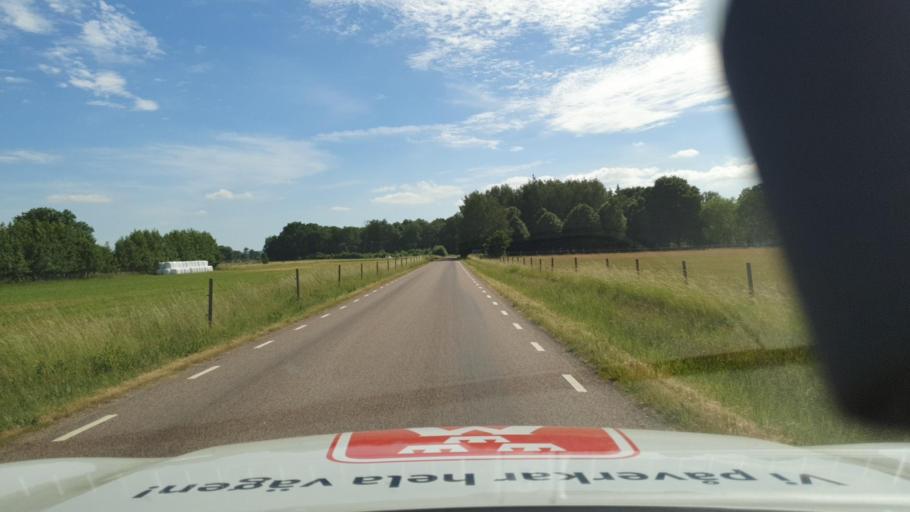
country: SE
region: Skane
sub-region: Sjobo Kommun
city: Blentarp
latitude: 55.6157
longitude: 13.6198
